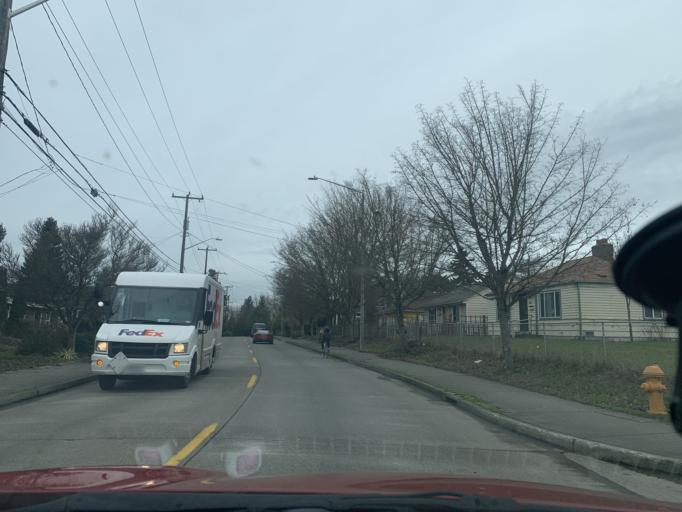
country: US
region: Washington
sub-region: King County
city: Bryn Mawr-Skyway
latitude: 47.5269
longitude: -122.2650
